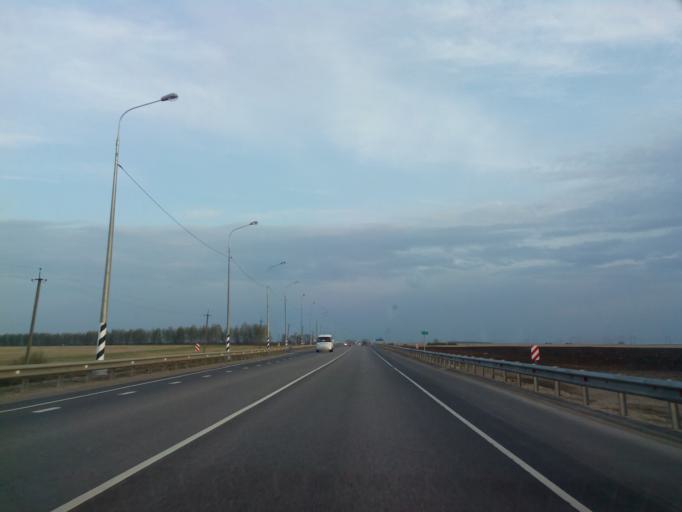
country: RU
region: Rjazan
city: Ryazhsk
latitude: 53.5830
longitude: 40.0413
